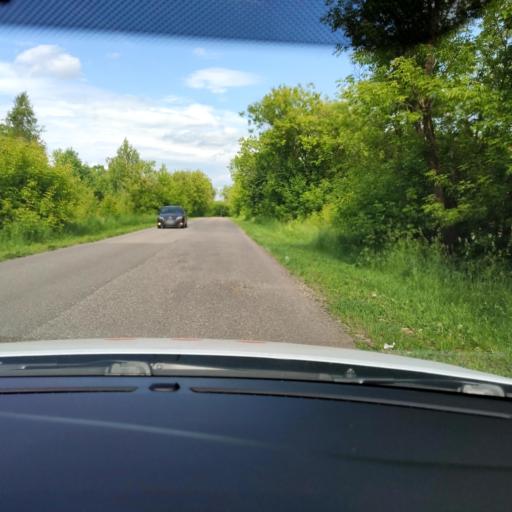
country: RU
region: Tatarstan
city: Stolbishchi
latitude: 55.7154
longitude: 49.2171
